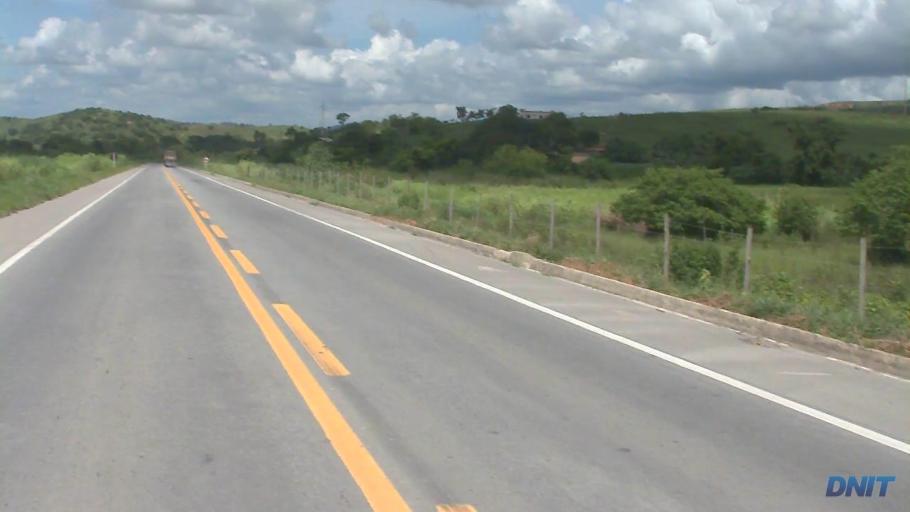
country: BR
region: Minas Gerais
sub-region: Governador Valadares
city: Governador Valadares
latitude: -18.9858
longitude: -42.1085
